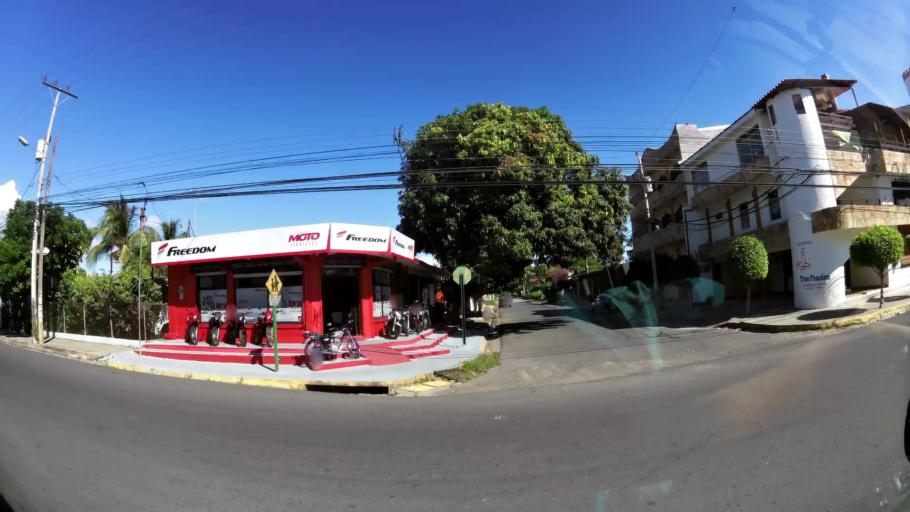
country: CR
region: Guanacaste
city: Liberia
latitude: 10.6357
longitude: -85.4323
